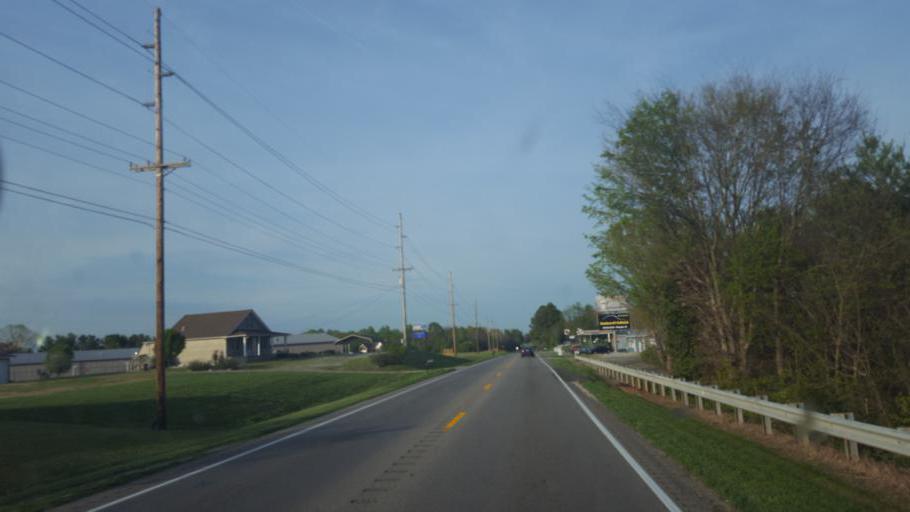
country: US
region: Kentucky
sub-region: Barren County
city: Glasgow
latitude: 36.9580
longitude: -85.9568
